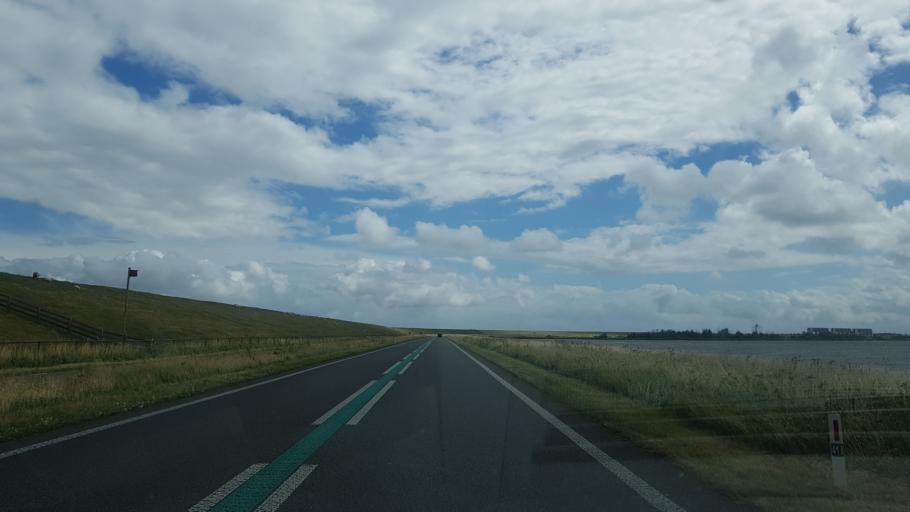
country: NL
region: Friesland
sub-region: Gemeente Dongeradeel
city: Anjum
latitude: 53.4115
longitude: 6.1684
